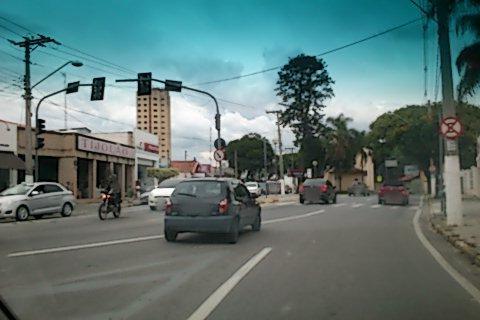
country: BR
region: Sao Paulo
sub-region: Jacarei
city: Jacarei
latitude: -23.2966
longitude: -45.9666
